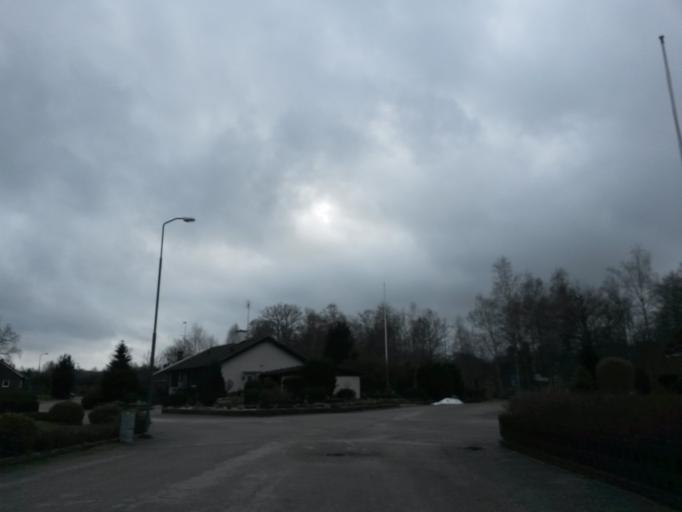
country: SE
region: Vaestra Goetaland
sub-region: Herrljunga Kommun
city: Herrljunga
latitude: 58.0749
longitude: 13.0141
